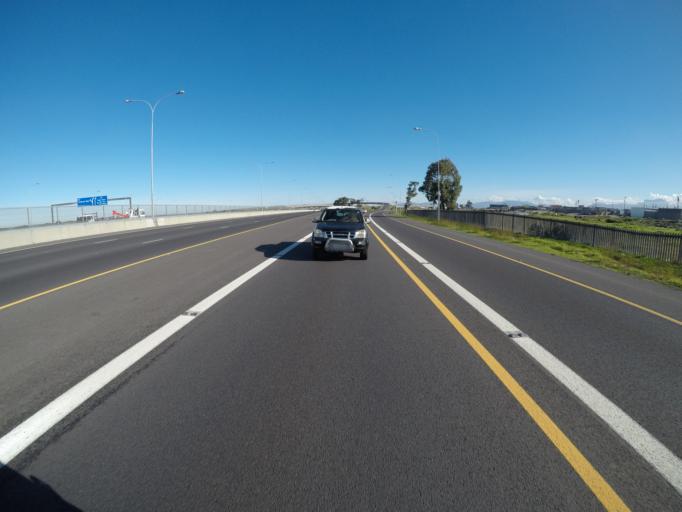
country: ZA
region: Western Cape
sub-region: City of Cape Town
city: Lansdowne
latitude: -33.9958
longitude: 18.6383
